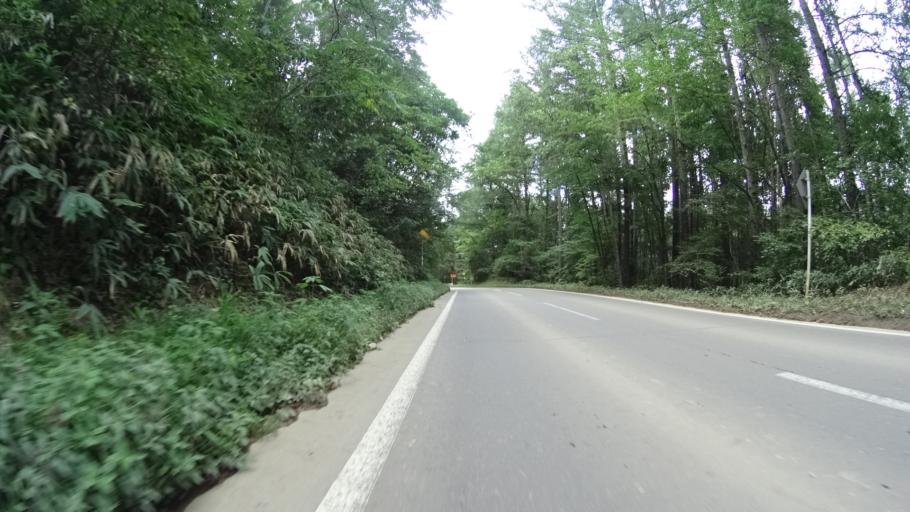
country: JP
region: Nagano
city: Saku
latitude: 35.9611
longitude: 138.5413
